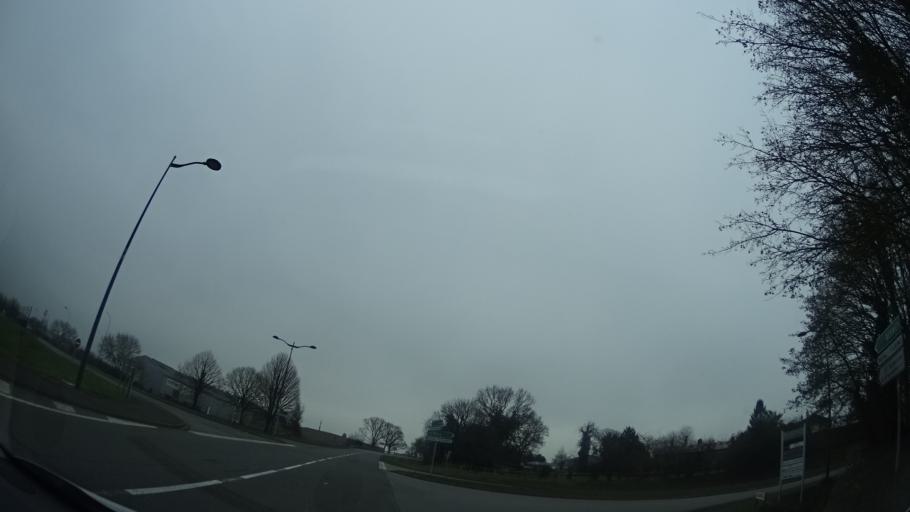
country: FR
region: Brittany
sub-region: Departement d'Ille-et-Vilaine
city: Brece
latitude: 48.1059
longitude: -1.4856
